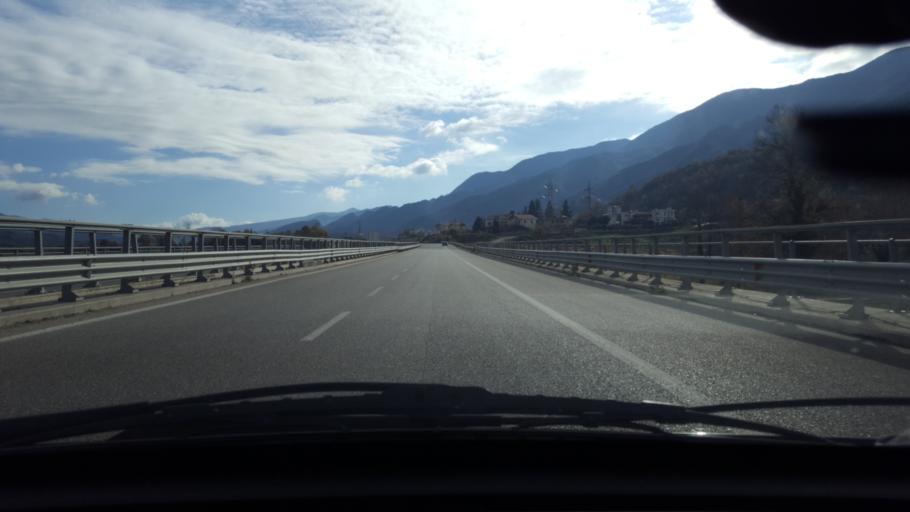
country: AL
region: Tirane
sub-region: Rrethi i Tiranes
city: Berzhite
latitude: 41.2566
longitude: 19.8908
